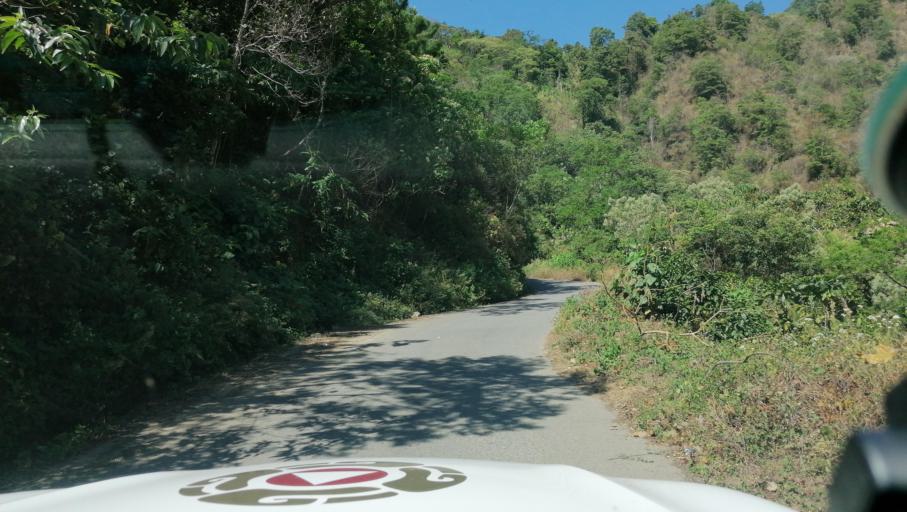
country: MX
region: Chiapas
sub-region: Cacahoatan
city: Benito Juarez
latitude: 15.1818
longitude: -92.1902
